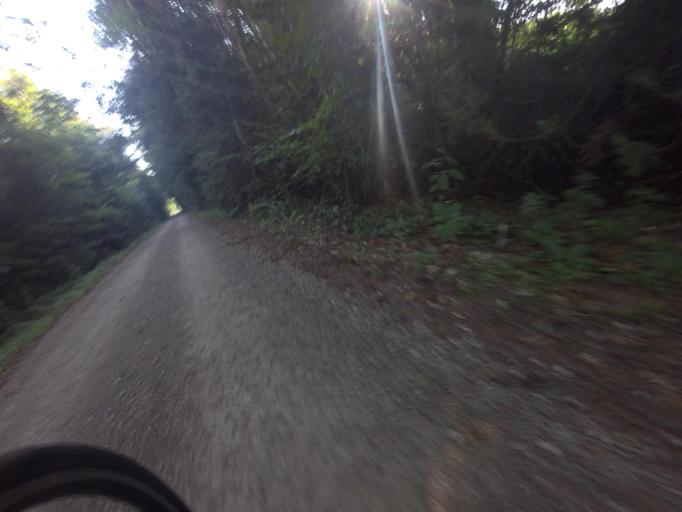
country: CA
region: Ontario
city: Goderich
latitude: 43.7588
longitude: -81.5461
